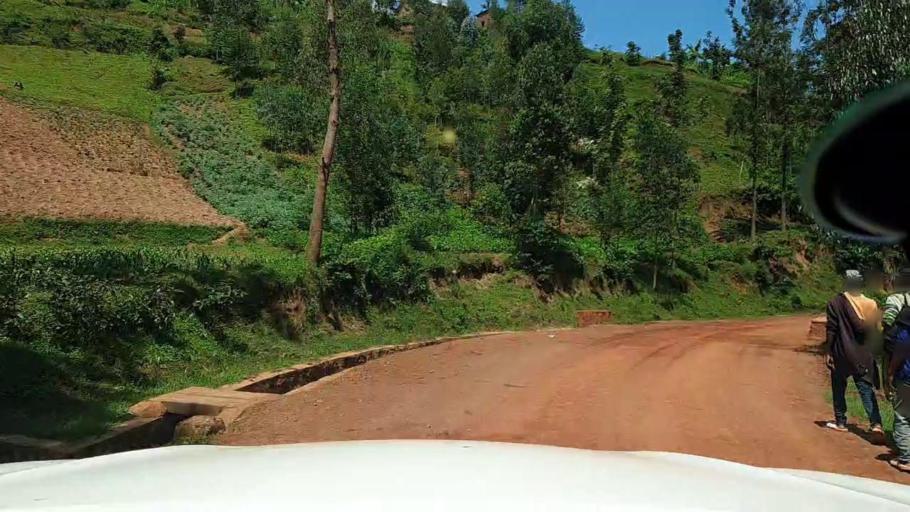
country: RW
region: Kigali
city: Kigali
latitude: -1.7764
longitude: 29.8740
